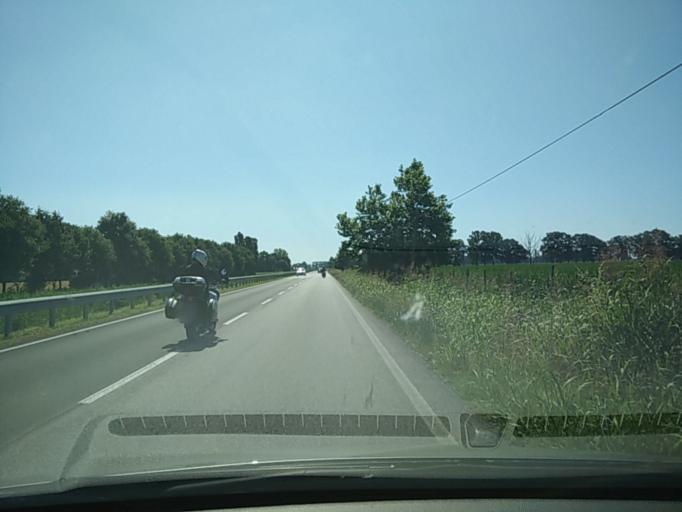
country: IT
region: Veneto
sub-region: Provincia di Venezia
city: San Giorgio di Livenza
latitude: 45.6251
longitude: 12.7893
